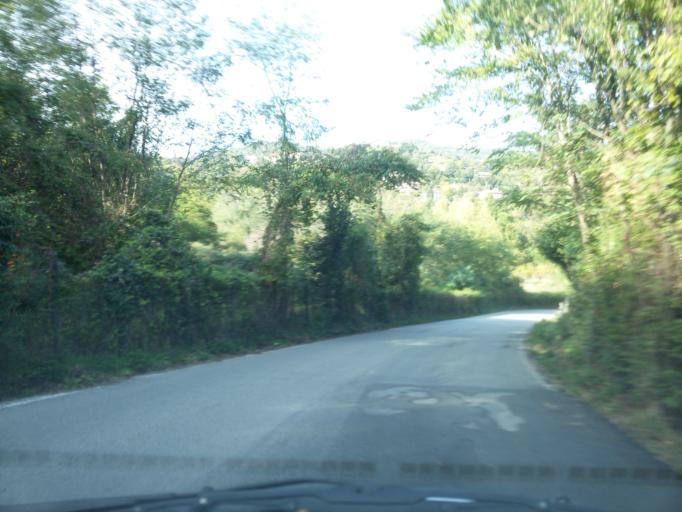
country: IT
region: Liguria
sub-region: Provincia di Genova
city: Piccarello
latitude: 44.4815
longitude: 8.9601
